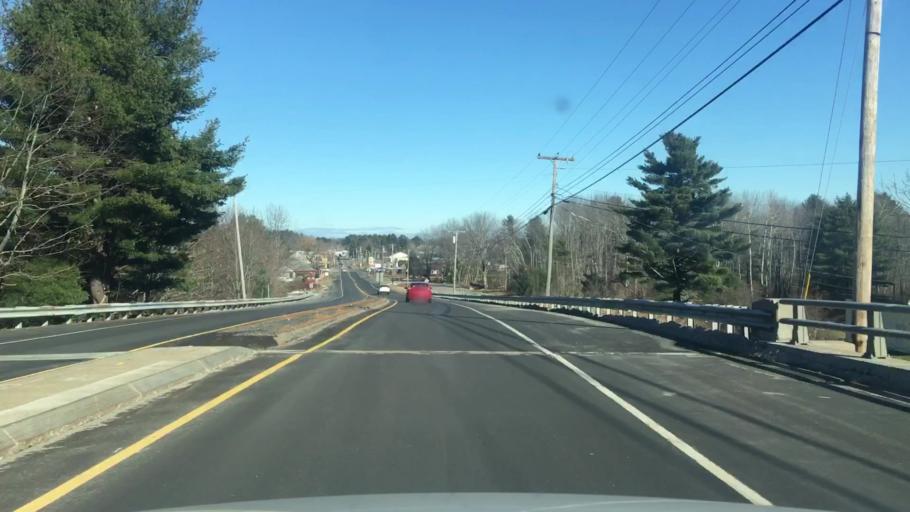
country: US
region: Maine
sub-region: York County
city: Biddeford
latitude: 43.4566
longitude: -70.4937
